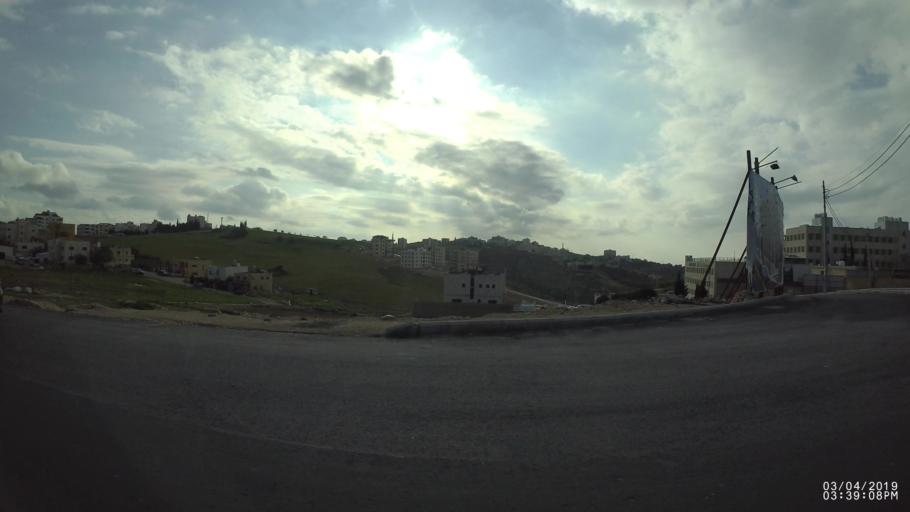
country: JO
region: Amman
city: Umm as Summaq
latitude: 31.9160
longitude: 35.8496
